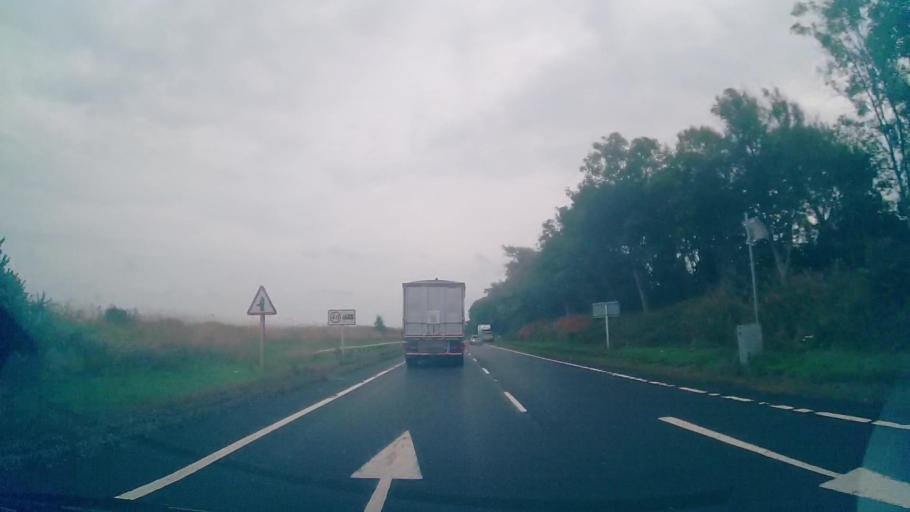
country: GB
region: Scotland
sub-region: Dumfries and Galloway
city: Gretna
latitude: 54.9945
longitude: -3.0988
